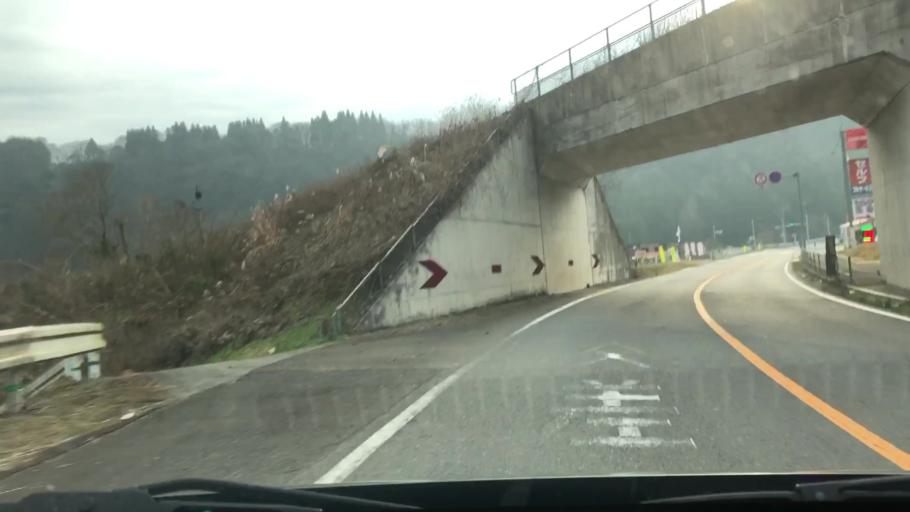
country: JP
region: Oita
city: Takedamachi
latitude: 32.9828
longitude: 131.5468
